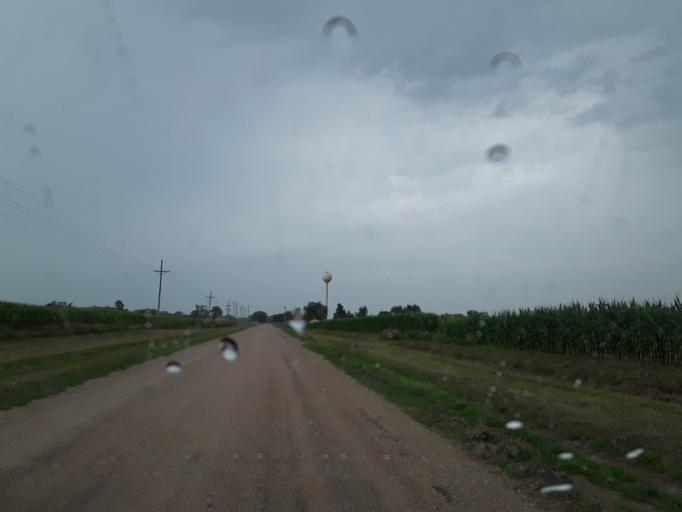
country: US
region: Nebraska
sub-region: Saunders County
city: Yutan
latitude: 41.1802
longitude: -96.4449
